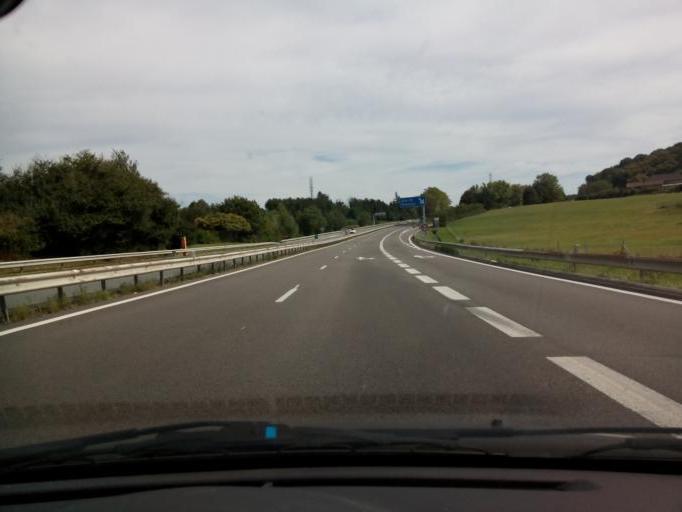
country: FR
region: Rhone-Alpes
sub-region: Departement de l'Isere
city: Saint-Victor-de-Cessieu
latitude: 45.5333
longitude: 5.4059
